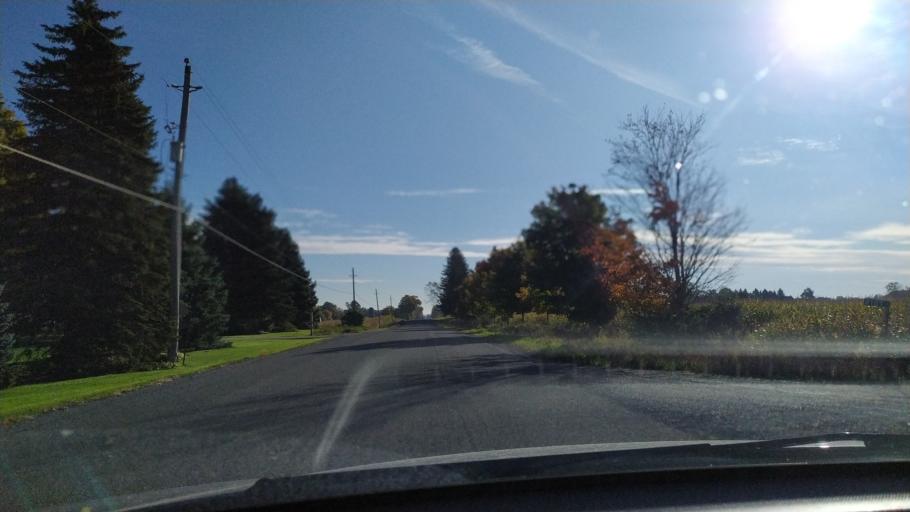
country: CA
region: Ontario
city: Stratford
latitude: 43.4619
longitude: -80.8327
